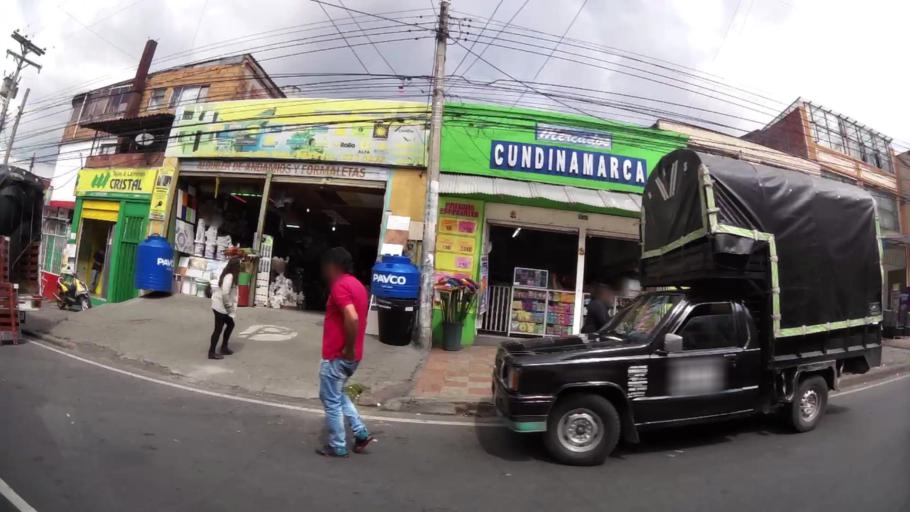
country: CO
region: Bogota D.C.
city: Bogota
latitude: 4.5678
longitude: -74.0936
